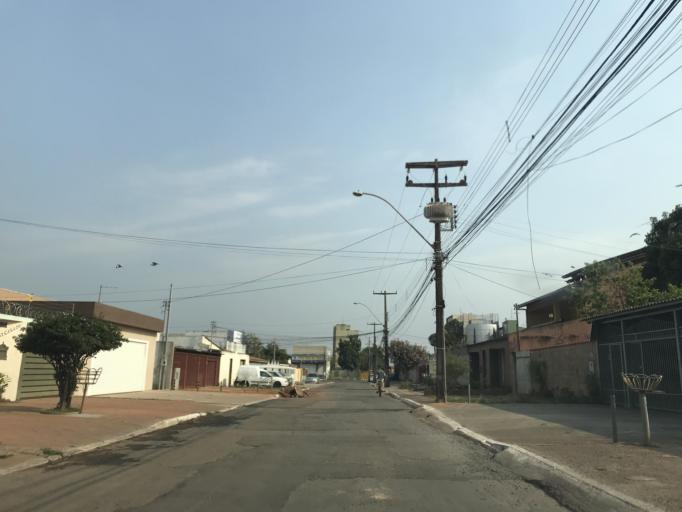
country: BR
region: Federal District
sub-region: Brasilia
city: Brasilia
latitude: -15.8031
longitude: -48.0632
